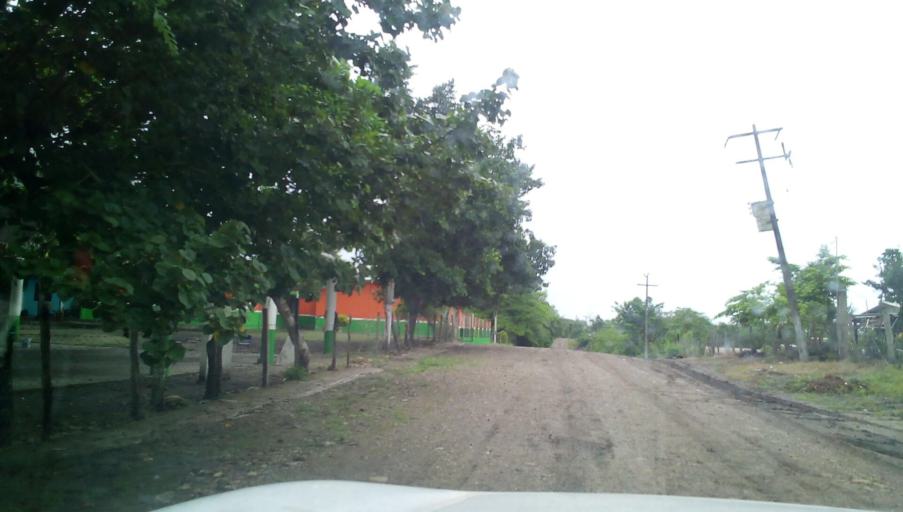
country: MX
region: Veracruz
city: Panuco
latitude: 21.8001
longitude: -98.1021
